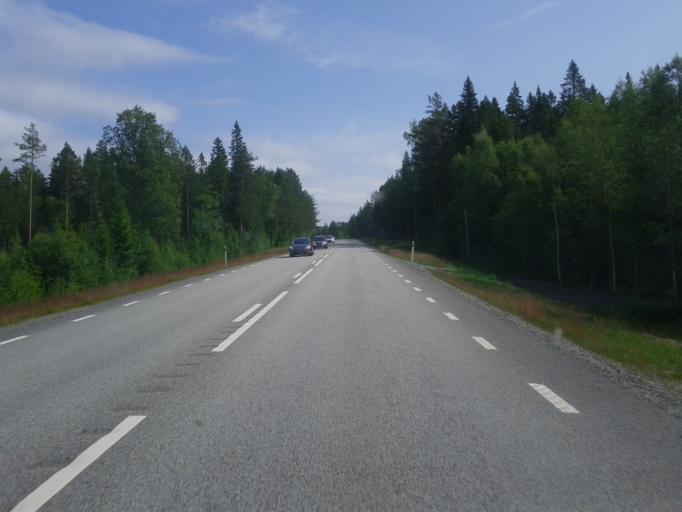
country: SE
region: Vaesterbotten
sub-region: Robertsfors Kommun
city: Robertsfors
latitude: 64.1812
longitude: 20.9779
